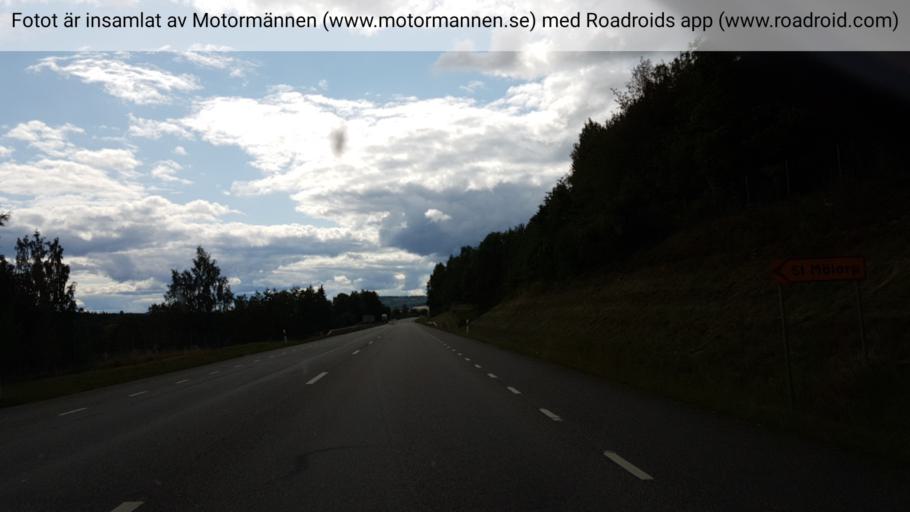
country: SE
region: Joenkoeping
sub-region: Tranas Kommun
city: Tranas
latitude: 58.0162
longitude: 14.9375
